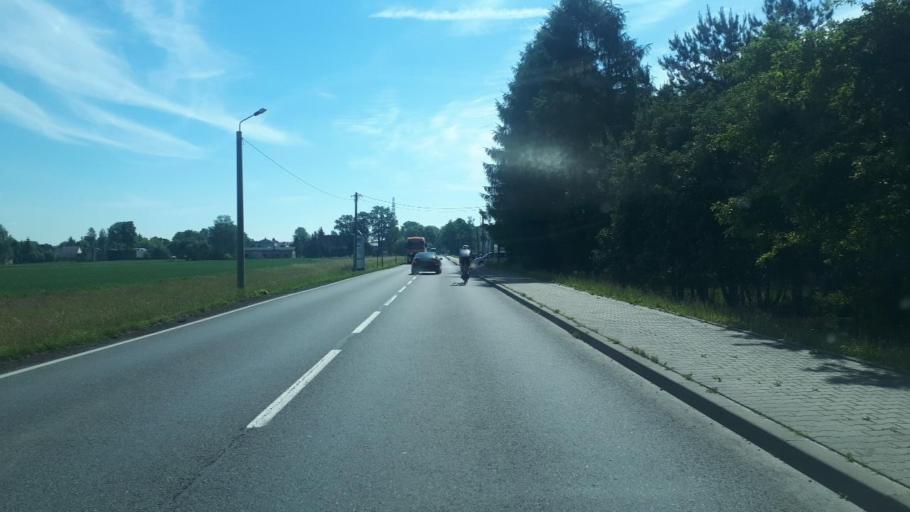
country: PL
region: Silesian Voivodeship
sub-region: Powiat pszczynski
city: Miedzna
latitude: 49.9689
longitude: 19.0441
